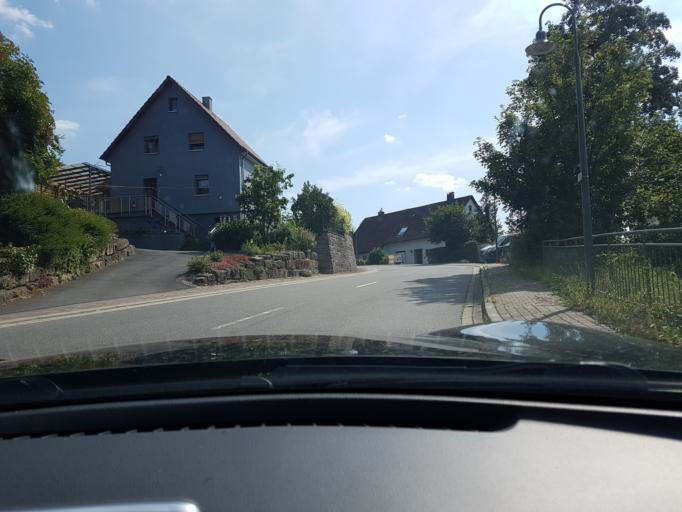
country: DE
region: Baden-Wuerttemberg
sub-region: Karlsruhe Region
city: Billigheim
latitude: 49.3497
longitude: 9.2599
